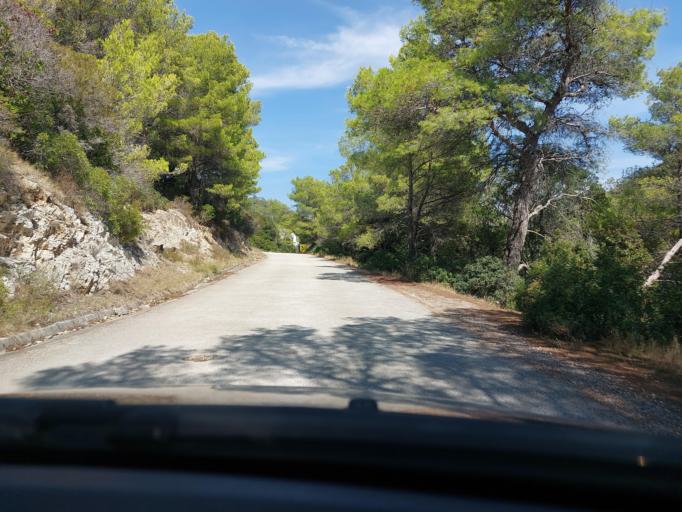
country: HR
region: Dubrovacko-Neretvanska
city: Smokvica
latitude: 42.7417
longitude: 16.8252
